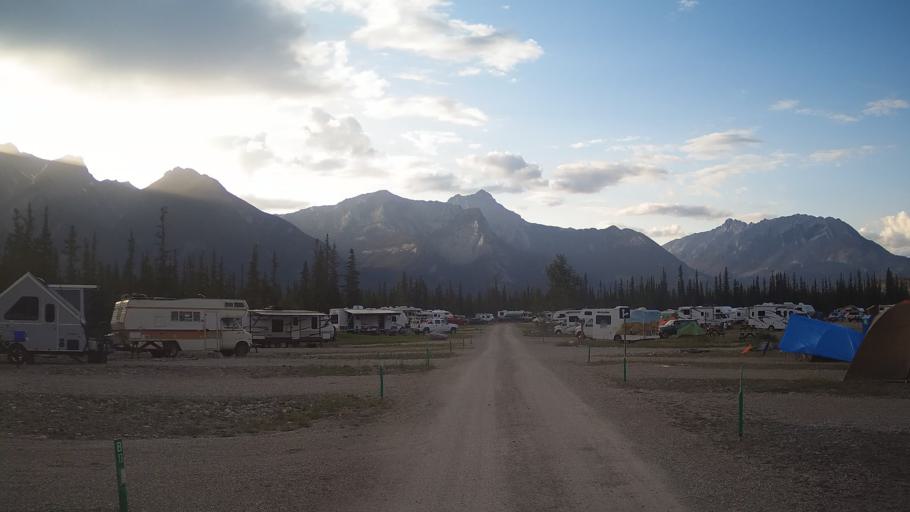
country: CA
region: Alberta
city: Jasper Park Lodge
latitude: 53.0163
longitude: -118.0872
